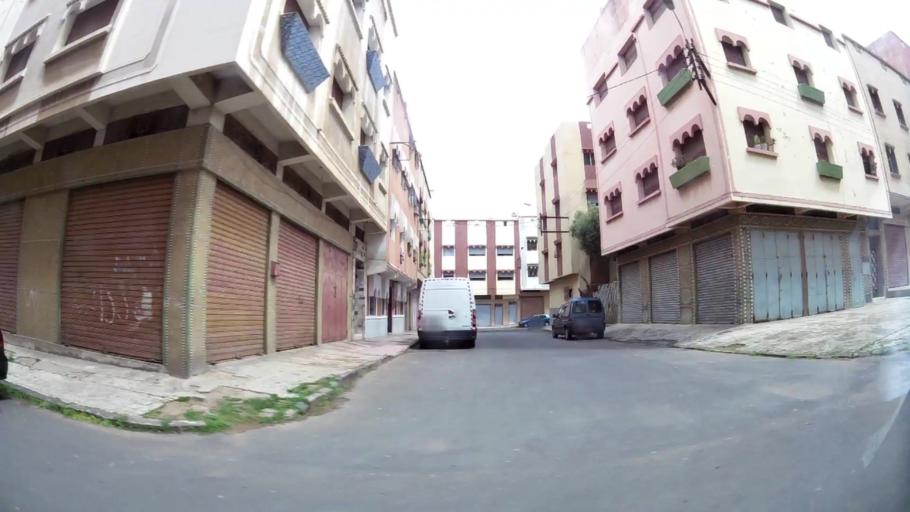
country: MA
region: Grand Casablanca
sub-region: Casablanca
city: Casablanca
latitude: 33.5385
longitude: -7.5850
